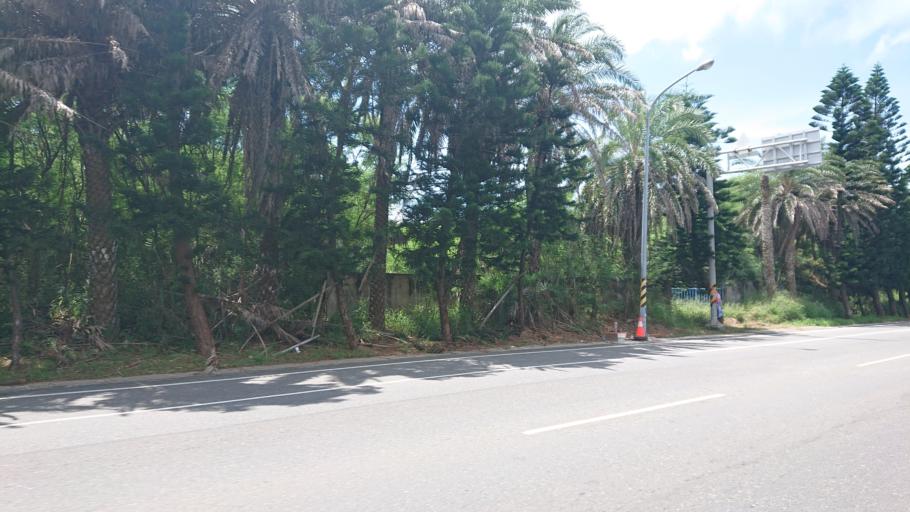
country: TW
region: Taiwan
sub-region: Penghu
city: Ma-kung
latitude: 23.5922
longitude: 119.6131
